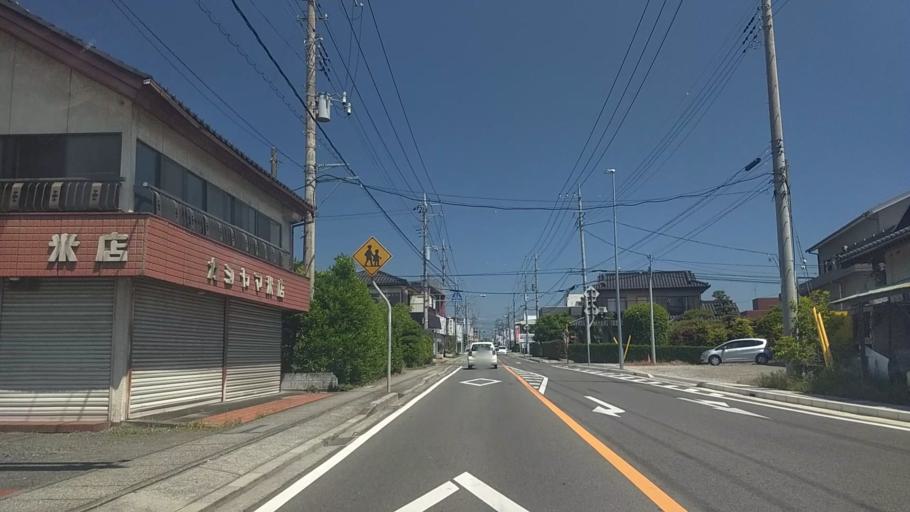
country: JP
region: Yamanashi
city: Ryuo
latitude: 35.6379
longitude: 138.4654
